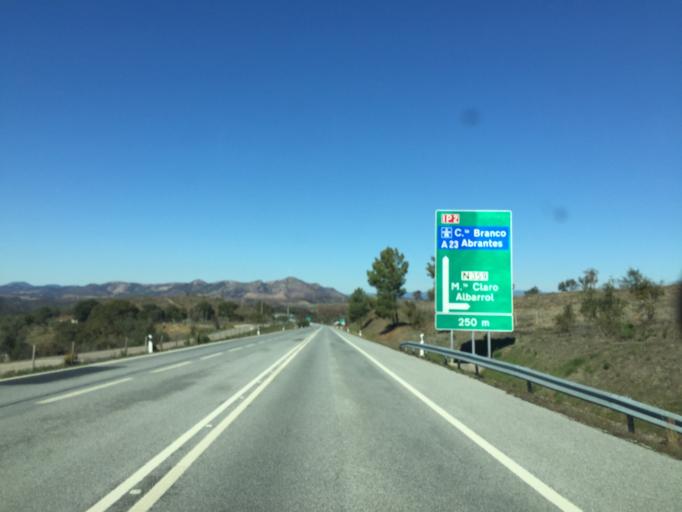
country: PT
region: Portalegre
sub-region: Nisa
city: Nisa
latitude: 39.5273
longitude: -7.7858
